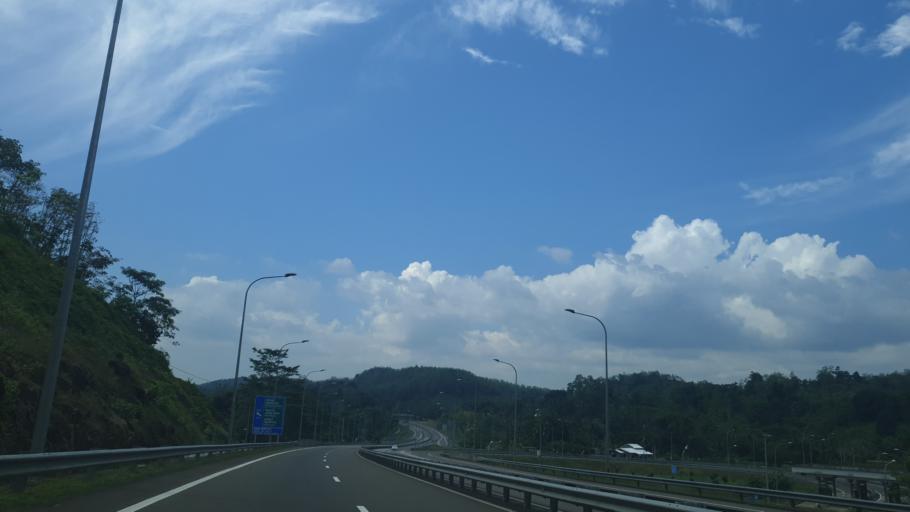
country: LK
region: Southern
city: Weligama
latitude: 6.0345
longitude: 80.3675
